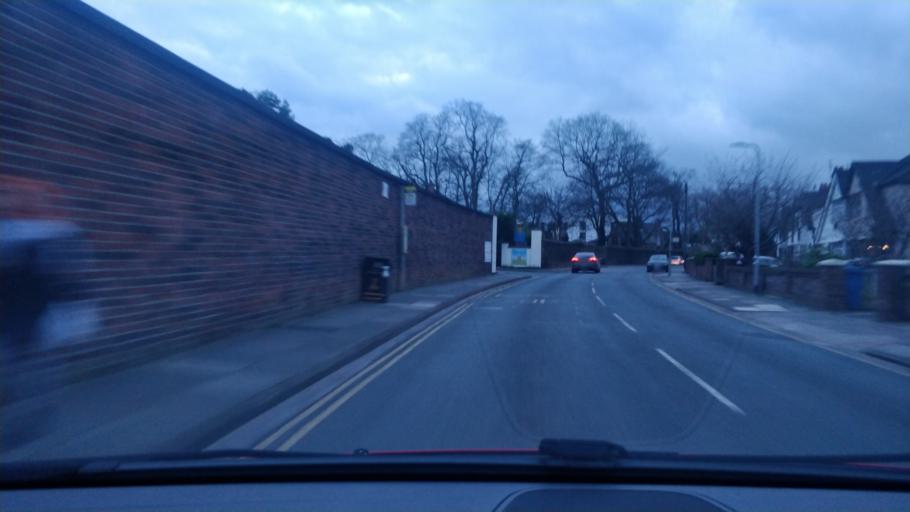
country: GB
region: England
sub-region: Knowsley
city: Knowsley
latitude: 53.4261
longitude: -2.8868
